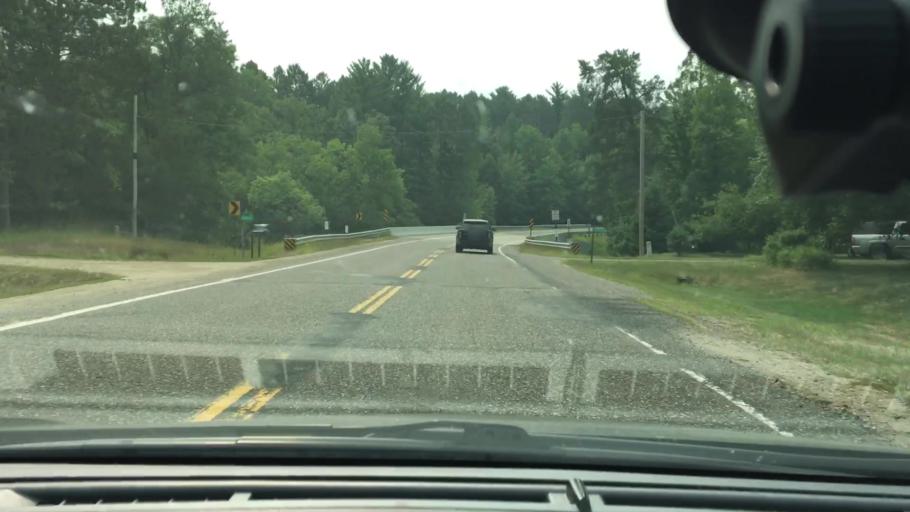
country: US
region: Minnesota
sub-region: Crow Wing County
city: Cross Lake
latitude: 46.6542
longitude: -94.0985
